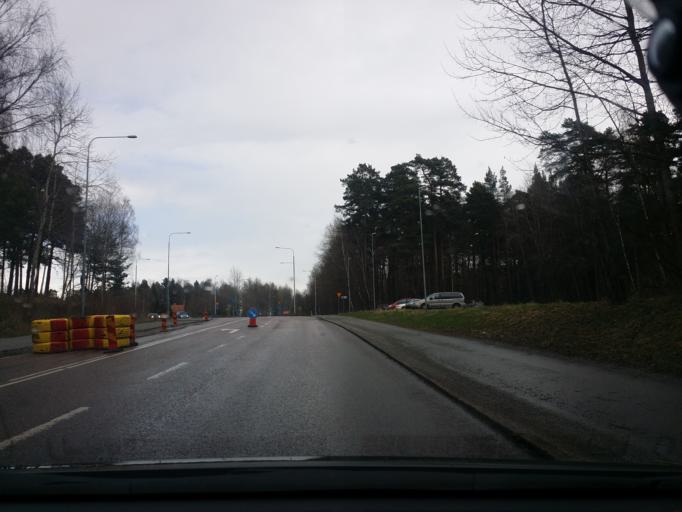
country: SE
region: Uppsala
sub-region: Enkopings Kommun
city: Enkoping
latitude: 59.6434
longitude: 17.1007
